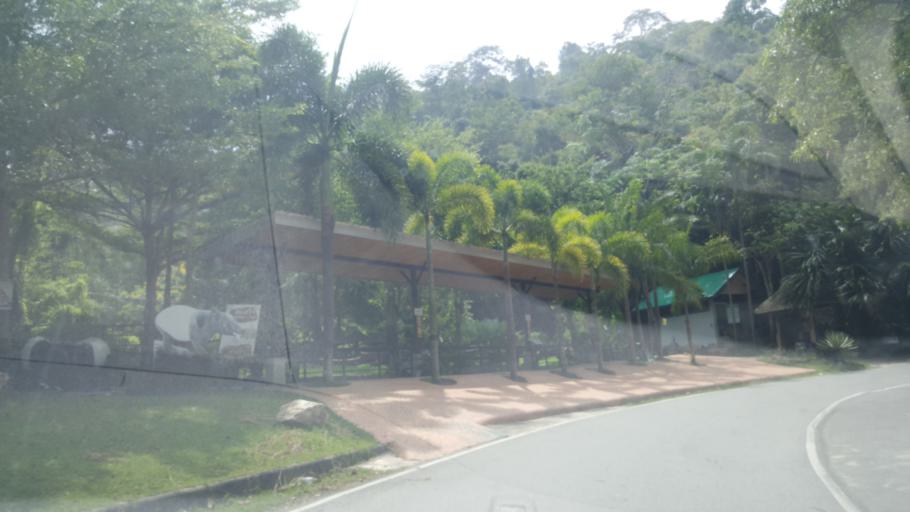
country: TH
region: Chon Buri
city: Ban Bueng
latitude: 13.2107
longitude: 101.0669
